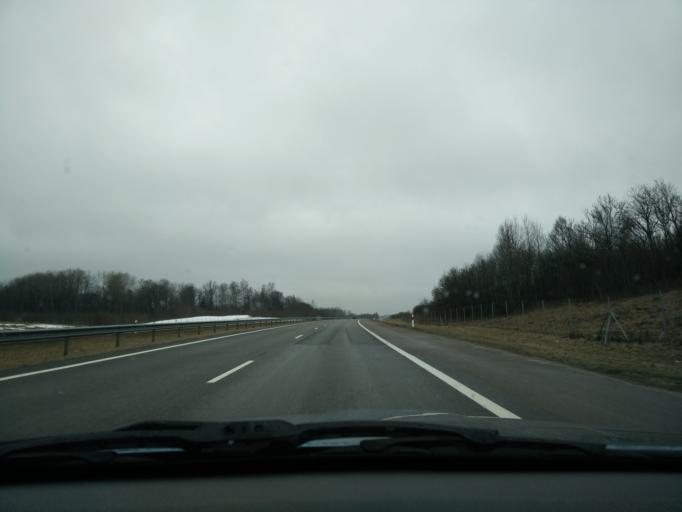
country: LT
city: Silale
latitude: 55.5409
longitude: 22.2896
